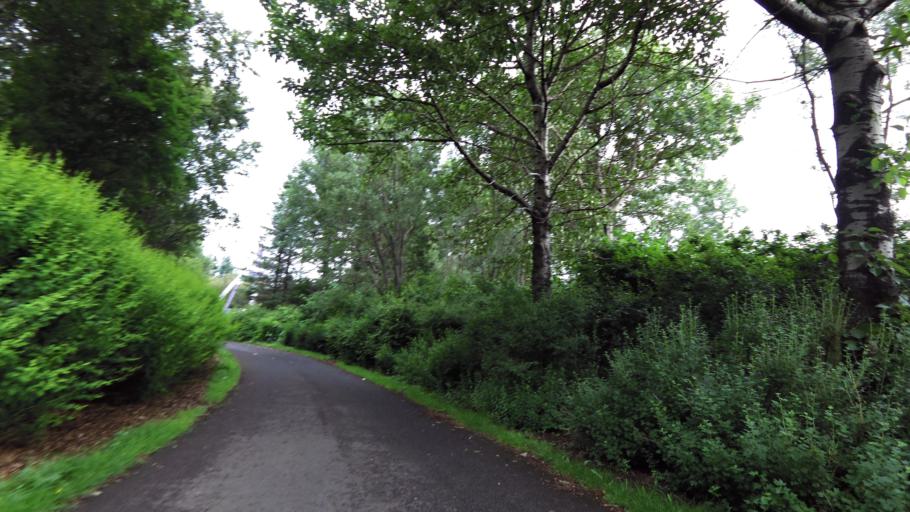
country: IS
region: Capital Region
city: Reykjavik
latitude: 64.1368
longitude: -21.8666
